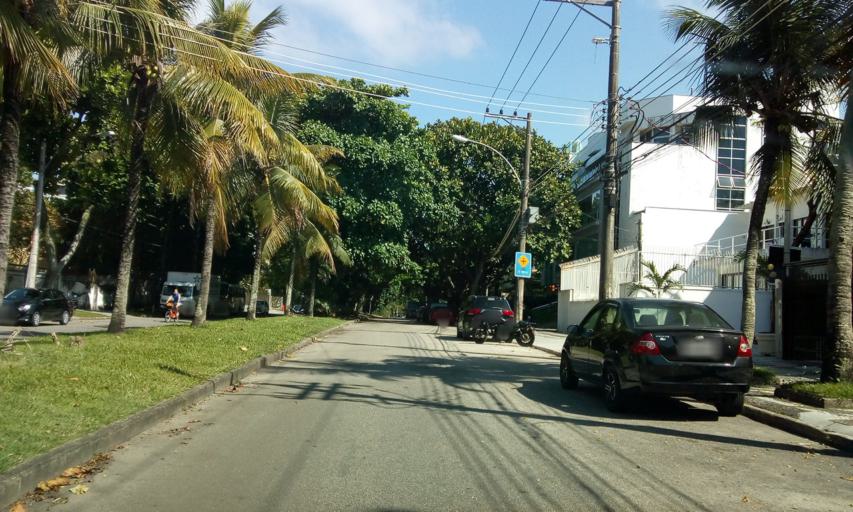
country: BR
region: Rio de Janeiro
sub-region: Rio De Janeiro
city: Rio de Janeiro
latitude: -23.0142
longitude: -43.3069
